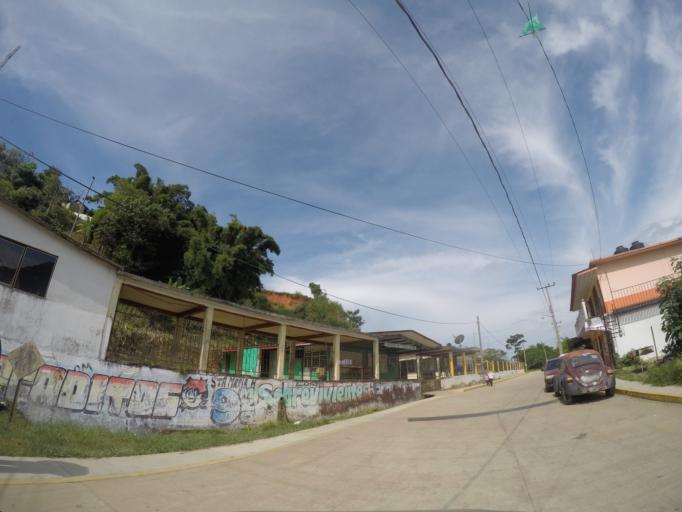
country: MX
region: Oaxaca
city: Pluma Hidalgo
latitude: 15.9261
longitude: -96.4182
